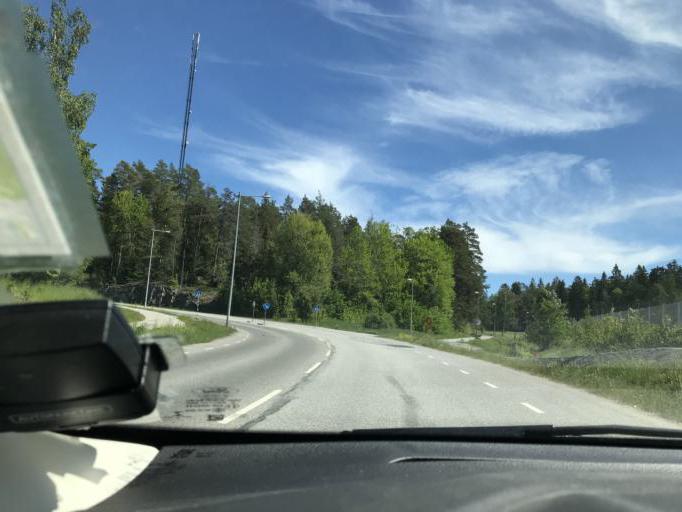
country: SE
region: Stockholm
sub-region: Botkyrka Kommun
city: Tumba
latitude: 59.2118
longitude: 17.8411
